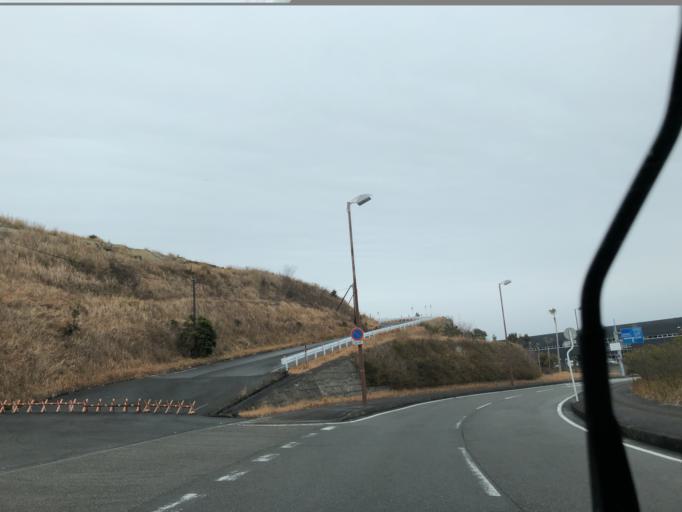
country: JP
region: Wakayama
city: Tanabe
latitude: 33.6635
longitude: 135.3590
